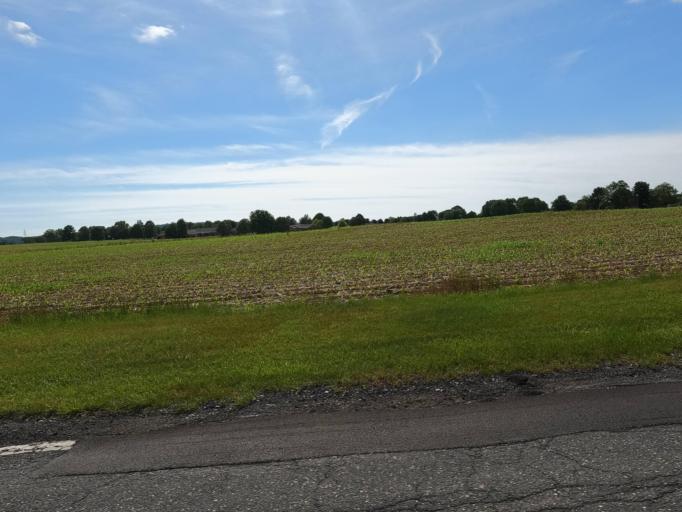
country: US
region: Pennsylvania
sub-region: Dauphin County
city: Palmdale
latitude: 40.2642
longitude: -76.6170
